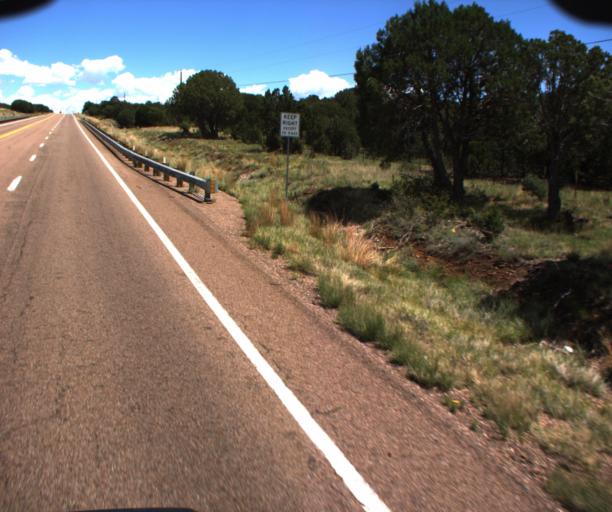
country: US
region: Arizona
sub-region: Apache County
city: Saint Johns
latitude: 34.2684
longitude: -109.5931
